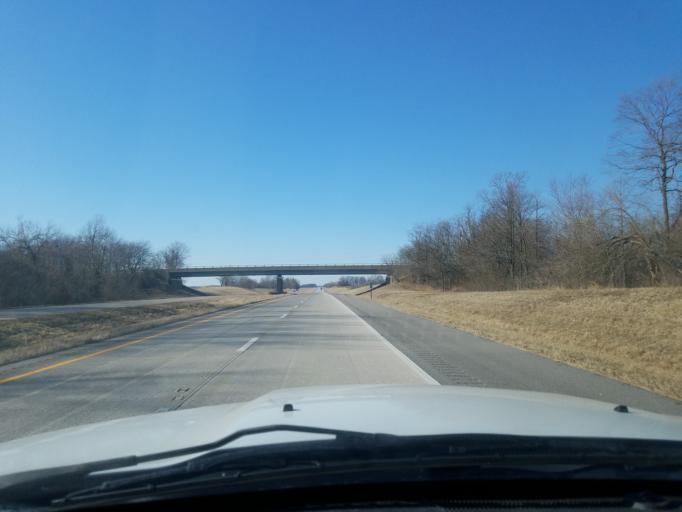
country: US
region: Kentucky
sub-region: Henderson County
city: Henderson
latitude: 37.7937
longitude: -87.4941
